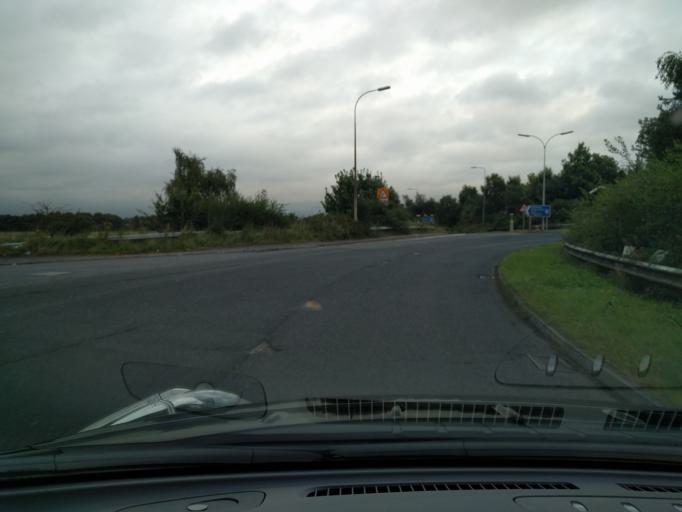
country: GB
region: England
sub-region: Warrington
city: Culcheth
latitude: 53.4358
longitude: -2.5000
